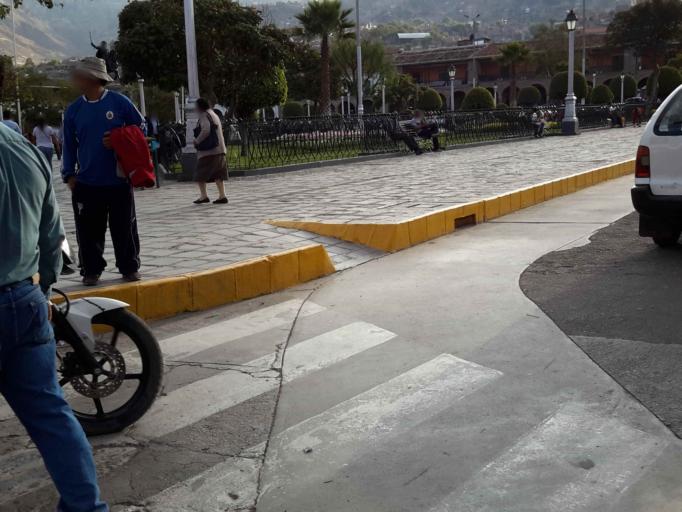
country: PE
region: Ayacucho
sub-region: Provincia de Huamanga
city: Ayacucho
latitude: -13.1599
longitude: -74.2252
